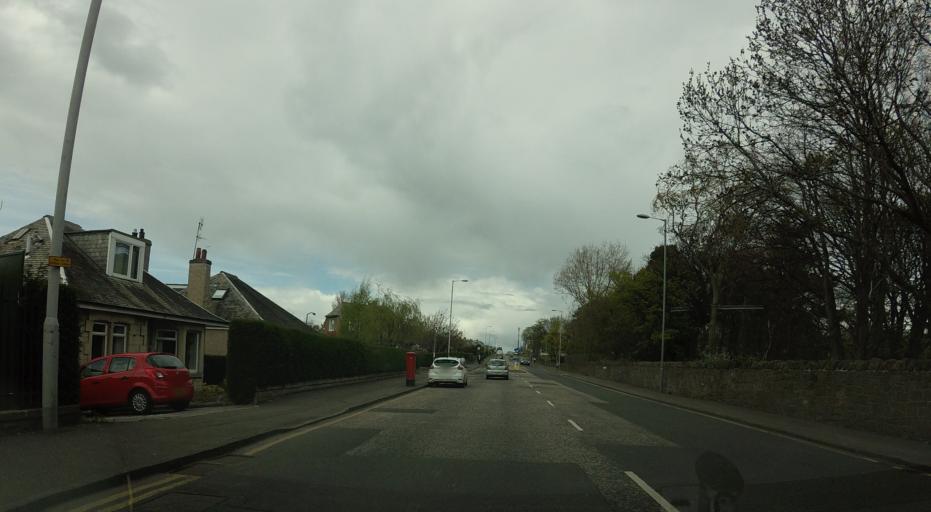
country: GB
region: Scotland
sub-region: Edinburgh
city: Edinburgh
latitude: 55.9642
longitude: -3.2330
